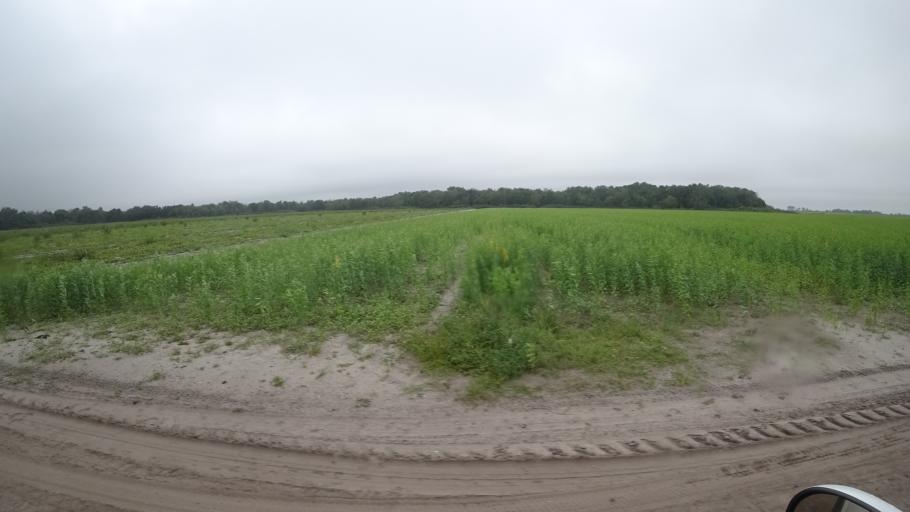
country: US
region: Florida
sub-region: Sarasota County
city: Warm Mineral Springs
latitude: 27.2876
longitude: -82.1584
